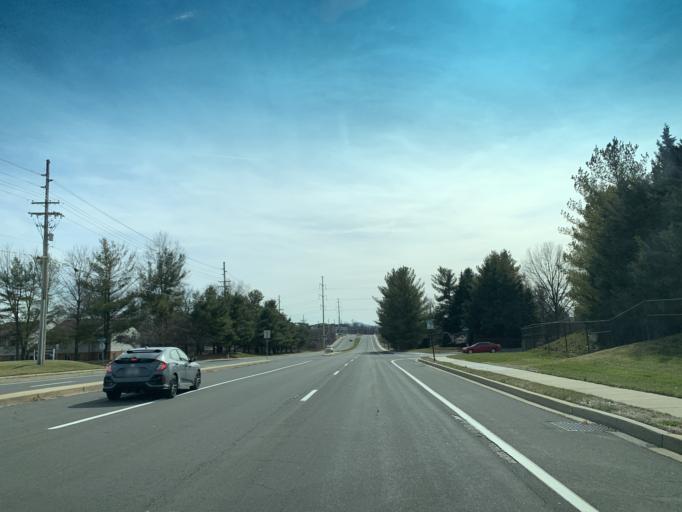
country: US
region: Maryland
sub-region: Frederick County
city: Ballenger Creek
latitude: 39.3866
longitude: -77.4224
